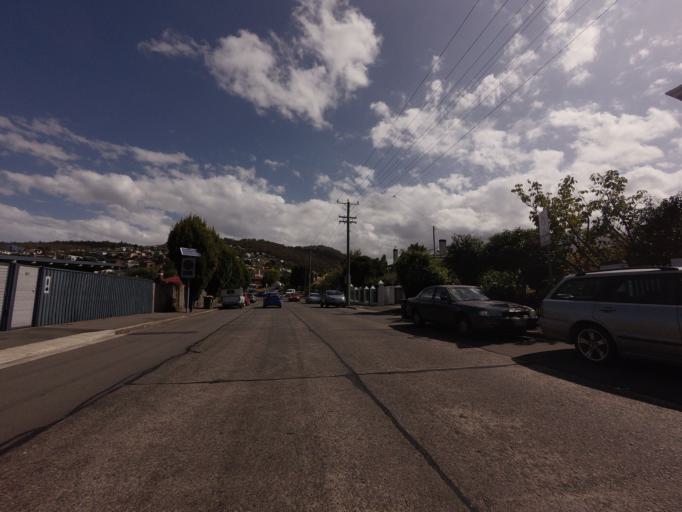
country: AU
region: Tasmania
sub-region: Hobart
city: Sandy Bay
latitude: -42.8979
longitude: 147.3179
